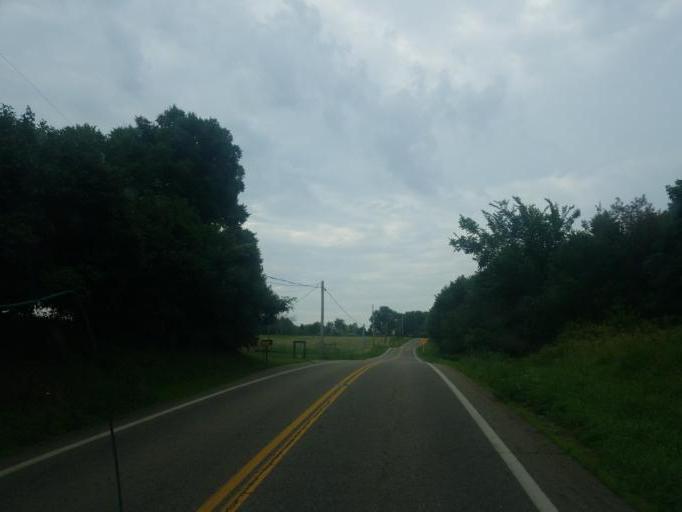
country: US
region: Ohio
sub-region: Carroll County
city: Lake Mohawk
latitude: 40.6474
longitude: -81.2318
